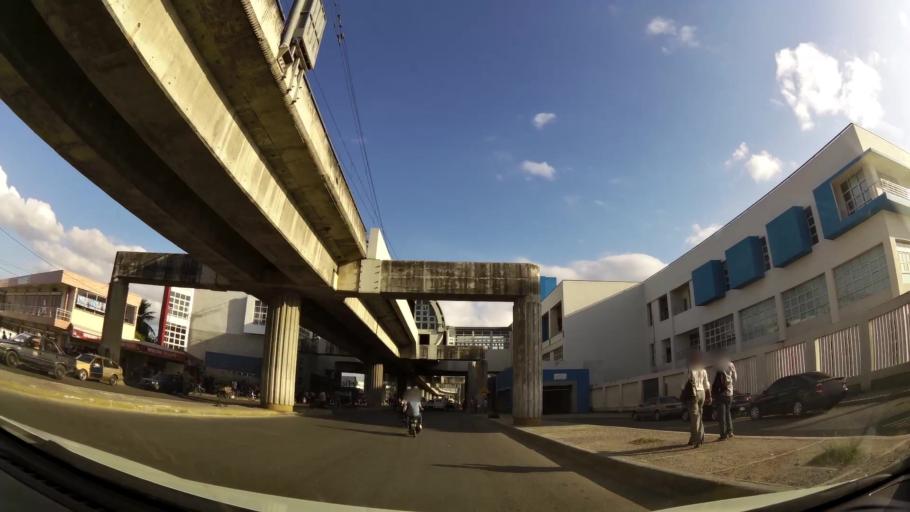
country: DO
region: Nacional
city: Ensanche Luperon
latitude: 18.5473
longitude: -69.9013
